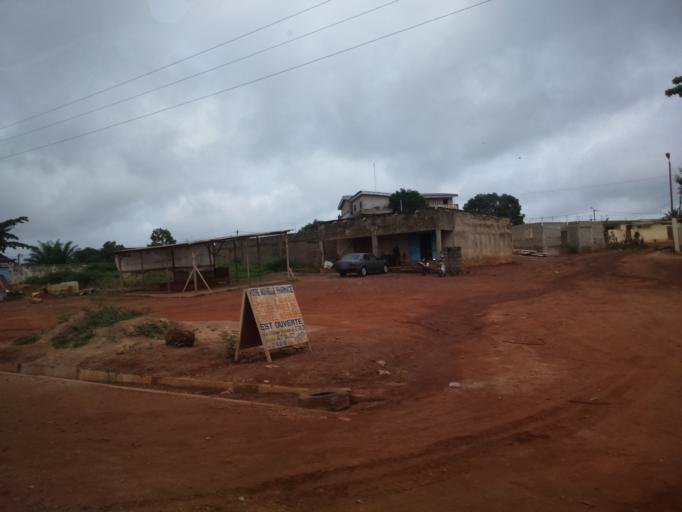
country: CI
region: Moyen-Comoe
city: Abengourou
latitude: 6.7248
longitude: -3.5058
